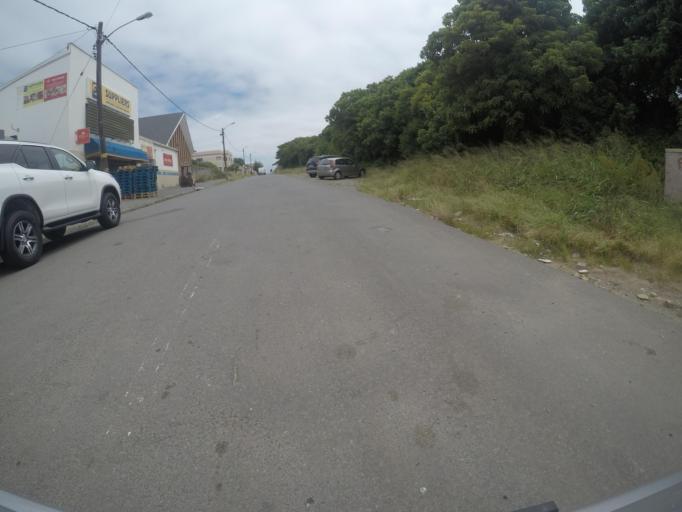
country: ZA
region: Eastern Cape
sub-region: Buffalo City Metropolitan Municipality
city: East London
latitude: -33.0124
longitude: 27.9147
